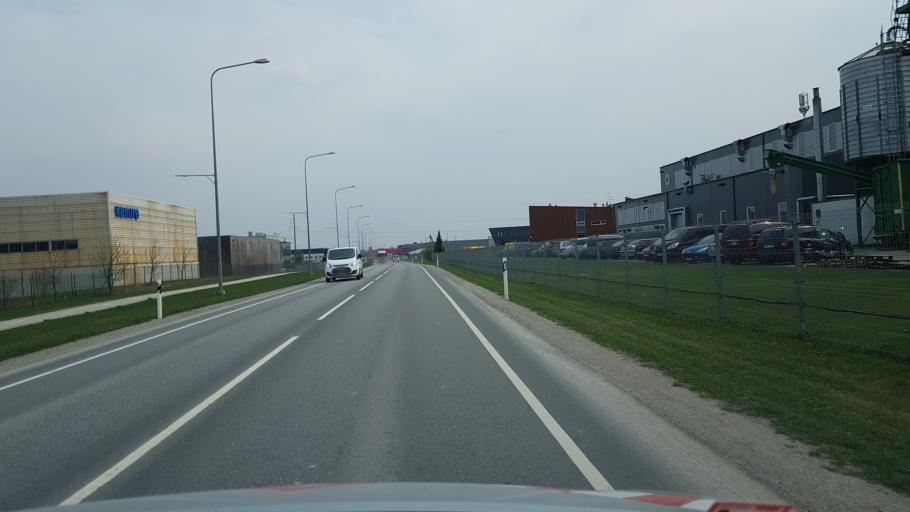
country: EE
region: Harju
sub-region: Rae vald
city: Jueri
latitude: 59.3634
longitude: 24.8767
